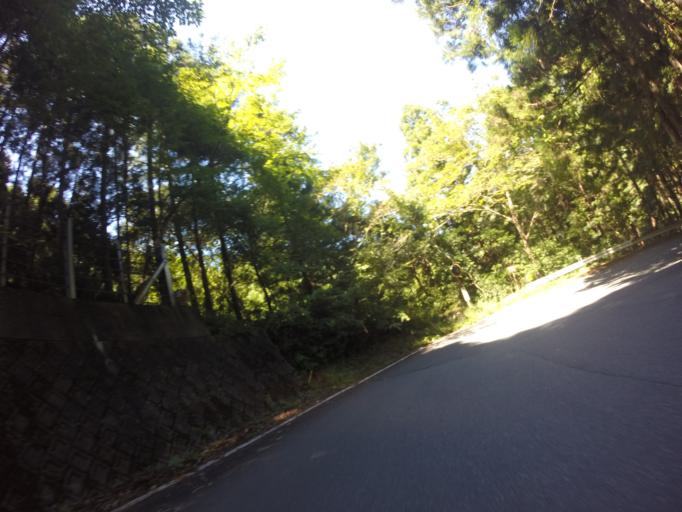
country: JP
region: Shizuoka
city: Fujieda
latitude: 34.9751
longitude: 138.2013
